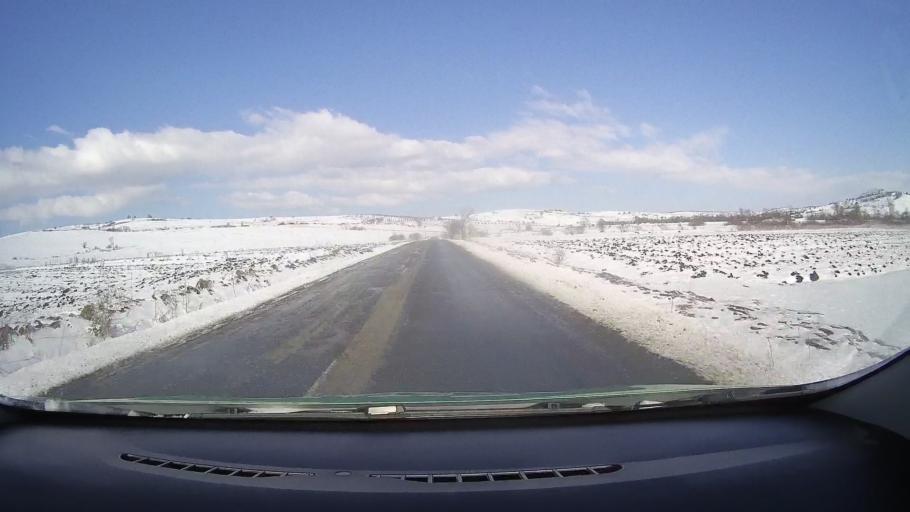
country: RO
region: Sibiu
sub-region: Comuna Vurpar
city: Vurpar
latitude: 45.8685
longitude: 24.3186
